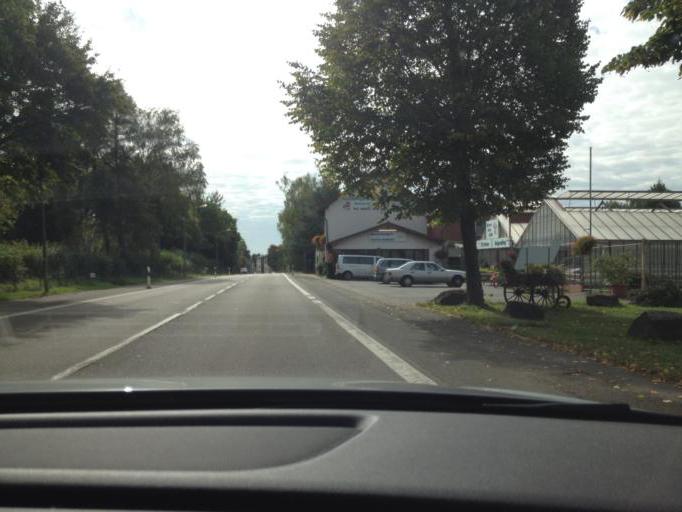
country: DE
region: Saarland
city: Schiffweiler
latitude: 49.3776
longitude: 7.1227
